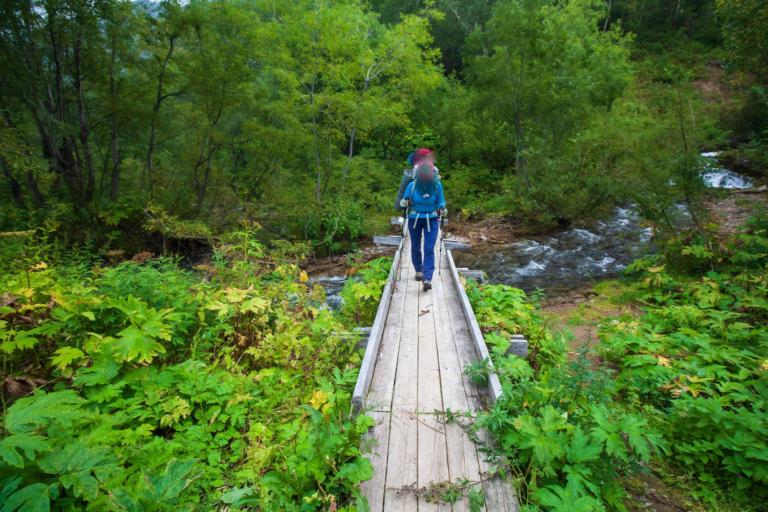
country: RU
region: Kamtsjatka
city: Yelizovo
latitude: 54.0507
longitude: 158.0421
